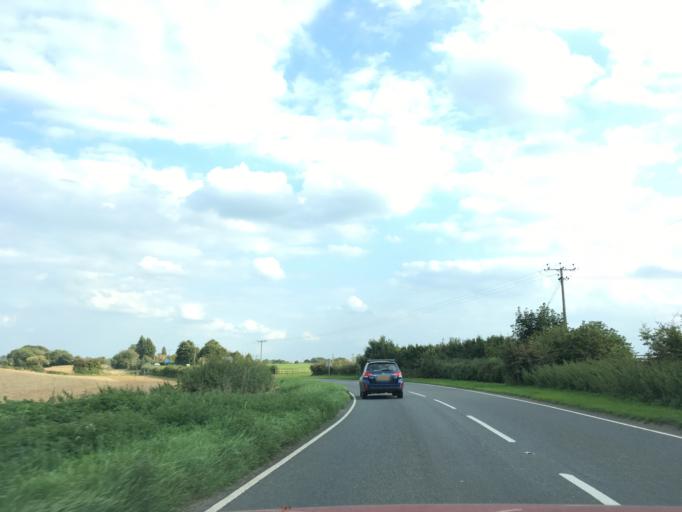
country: GB
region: England
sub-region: Gloucestershire
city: Nailsworth
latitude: 51.6489
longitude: -2.2255
